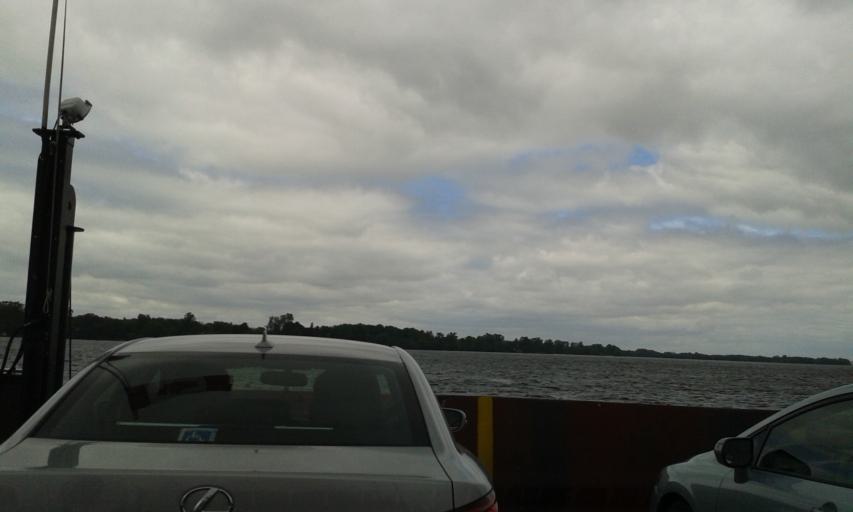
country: CA
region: Ontario
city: Picton
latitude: 44.0424
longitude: -77.0573
